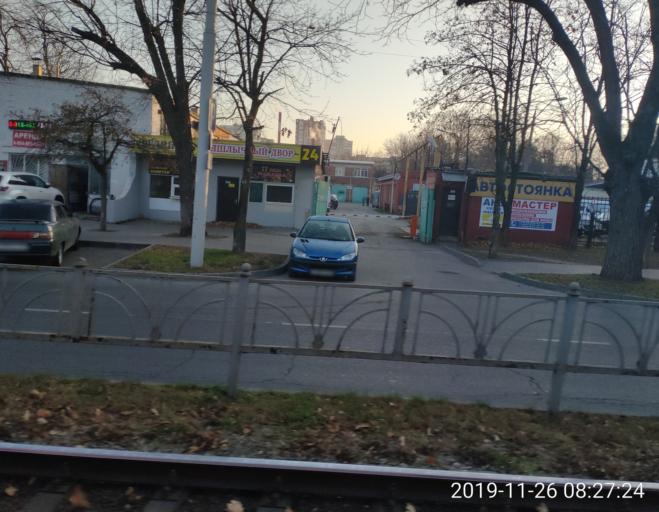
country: RU
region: Krasnodarskiy
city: Krasnodar
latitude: 45.0571
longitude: 39.0024
